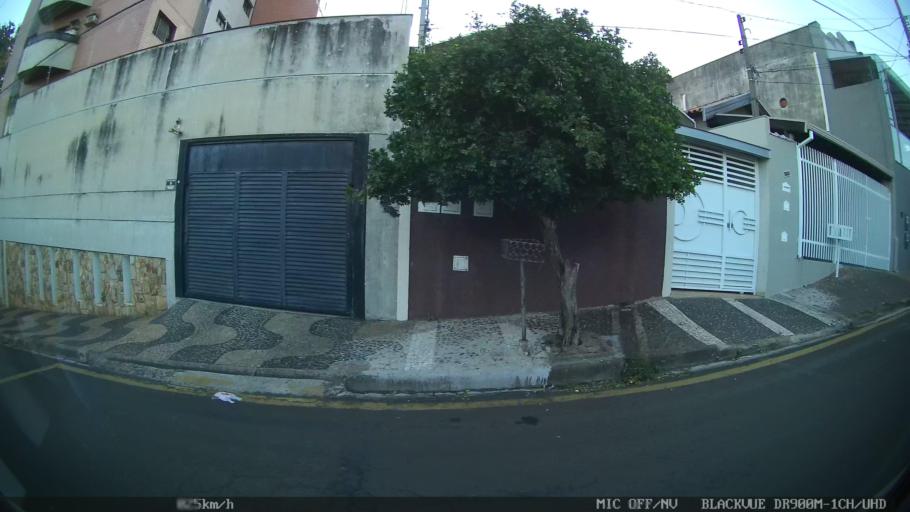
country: BR
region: Sao Paulo
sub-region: Santa Barbara D'Oeste
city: Santa Barbara d'Oeste
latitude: -22.7580
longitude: -47.4178
